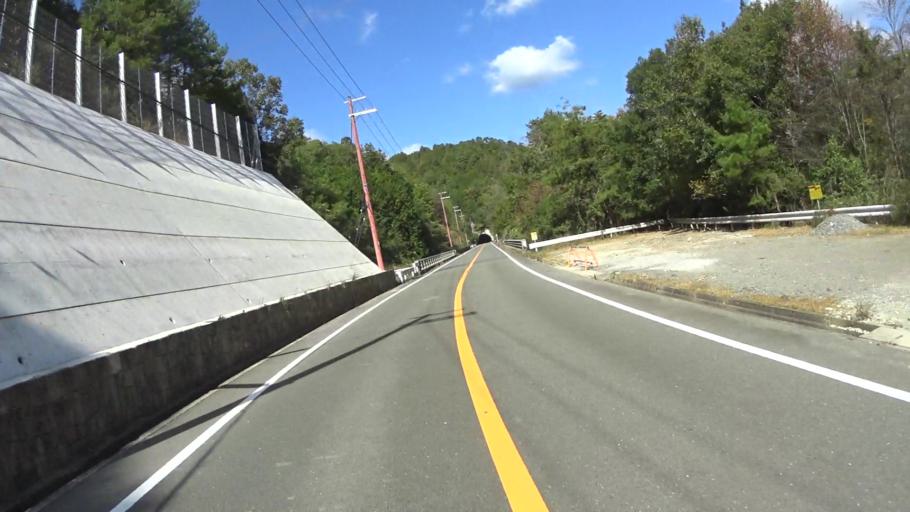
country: JP
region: Kyoto
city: Kameoka
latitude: 35.1344
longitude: 135.5355
